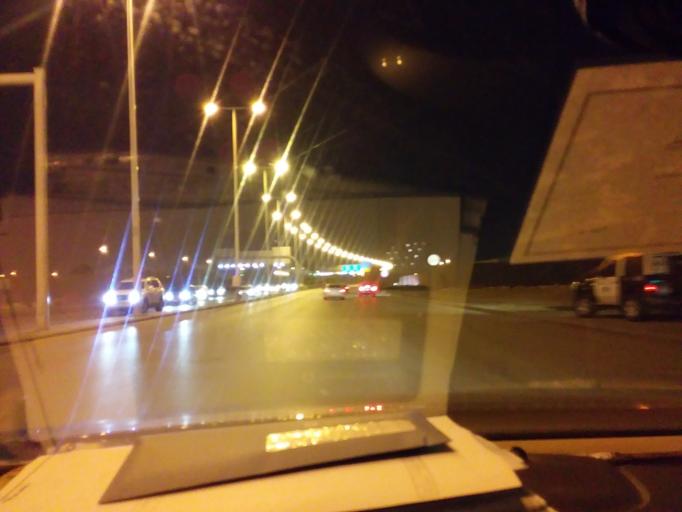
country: SA
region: Ar Riyad
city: Riyadh
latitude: 24.7213
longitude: 46.6933
